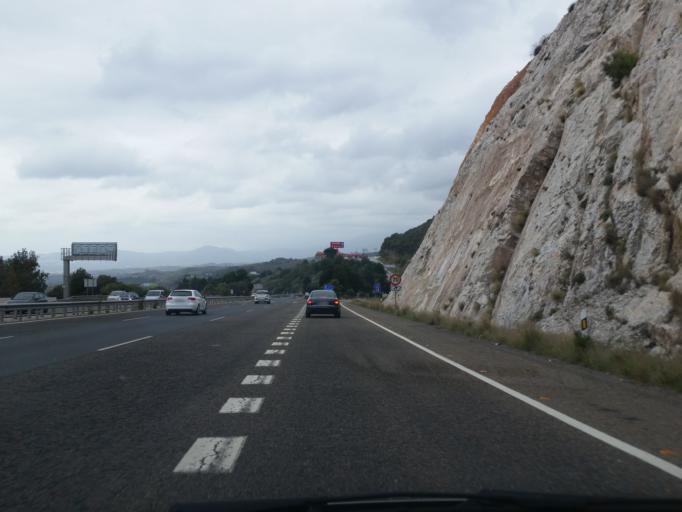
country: ES
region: Andalusia
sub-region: Provincia de Malaga
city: Benalmadena
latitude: 36.5873
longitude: -4.5917
